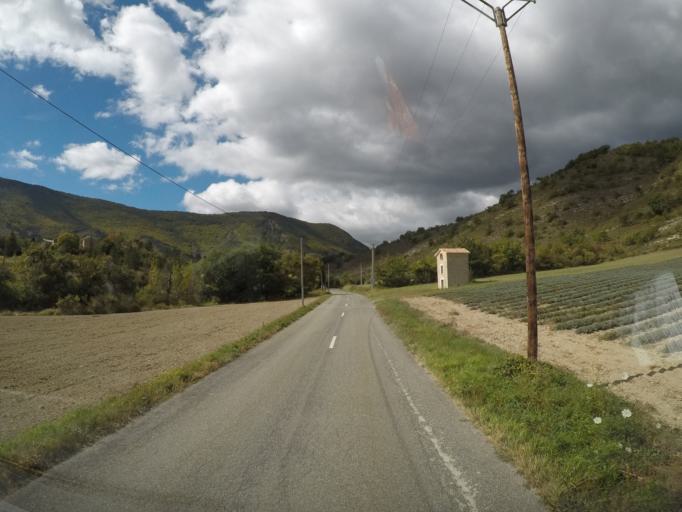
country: FR
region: Provence-Alpes-Cote d'Azur
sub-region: Departement du Vaucluse
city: Sault
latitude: 44.1731
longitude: 5.6029
